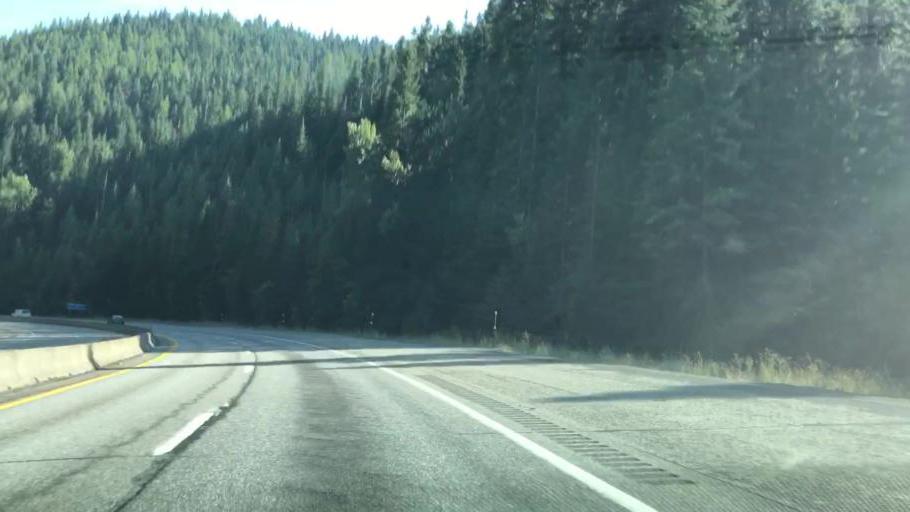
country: US
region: Idaho
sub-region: Shoshone County
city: Pinehurst
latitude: 47.5924
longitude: -116.4928
